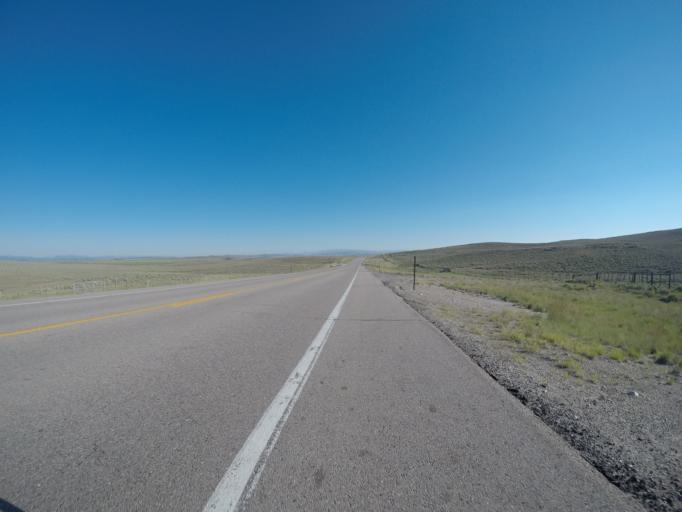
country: US
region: Wyoming
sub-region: Sublette County
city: Pinedale
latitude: 42.9163
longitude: -110.0791
